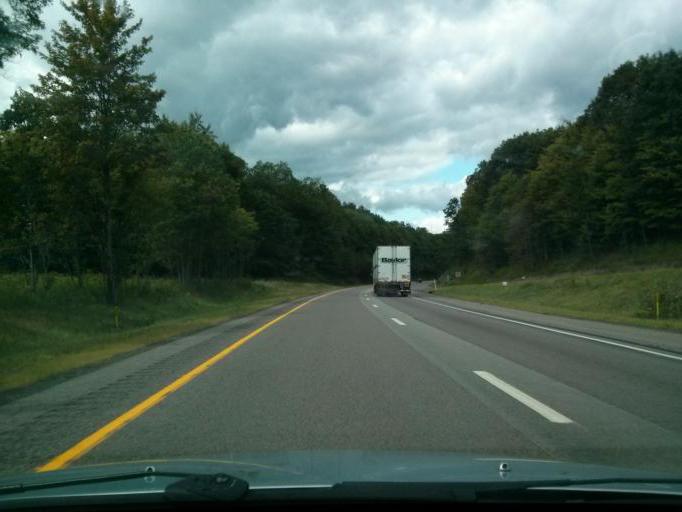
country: US
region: Pennsylvania
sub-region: Jefferson County
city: Reynoldsville
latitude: 41.1380
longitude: -78.9671
